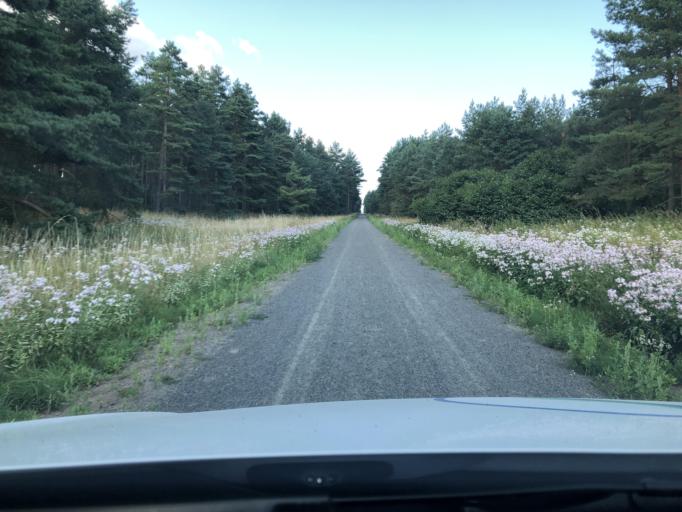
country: SE
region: Skane
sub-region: Kristianstads Kommun
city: Norra Asum
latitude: 55.9229
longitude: 14.1251
